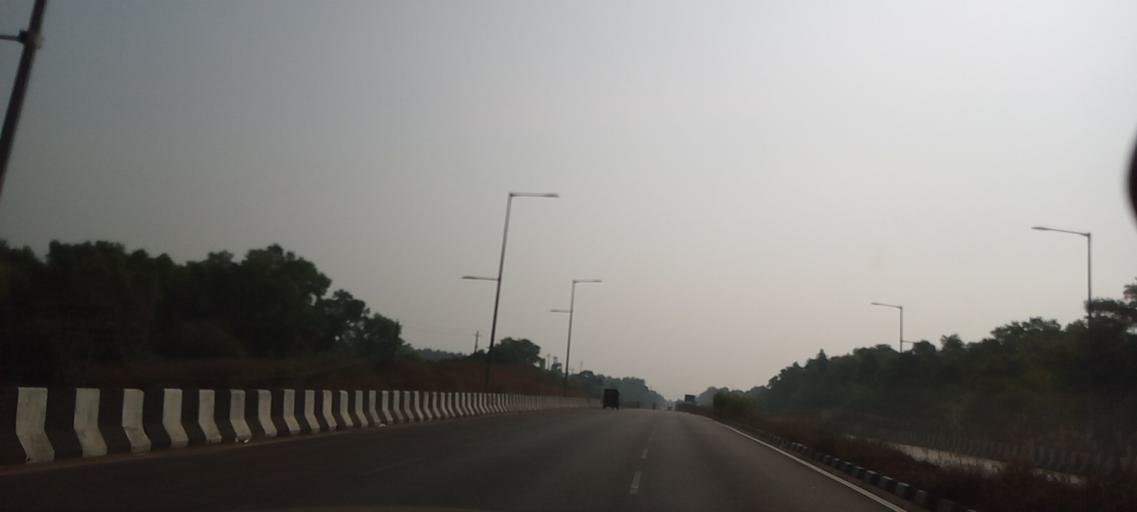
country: IN
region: Karnataka
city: Gangolli
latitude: 13.6882
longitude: 74.6606
